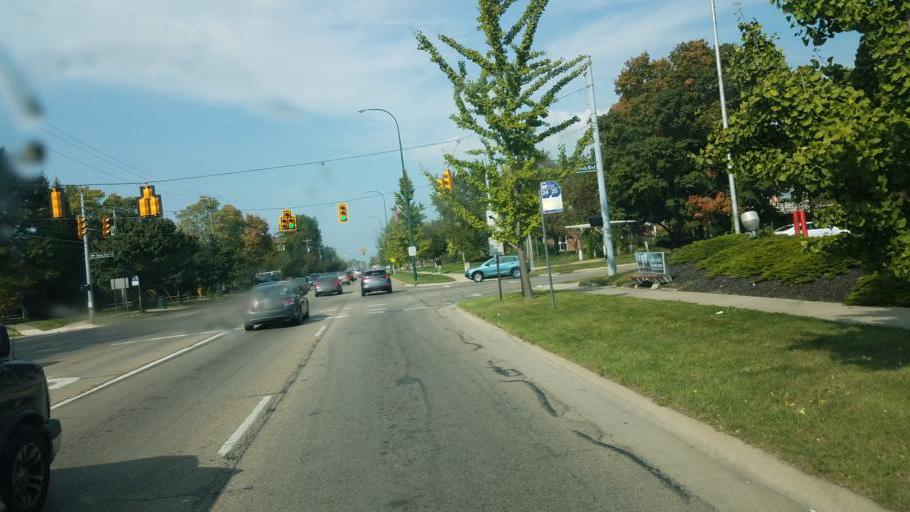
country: US
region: Ohio
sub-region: Franklin County
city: Gahanna
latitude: 40.0131
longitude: -82.8669
